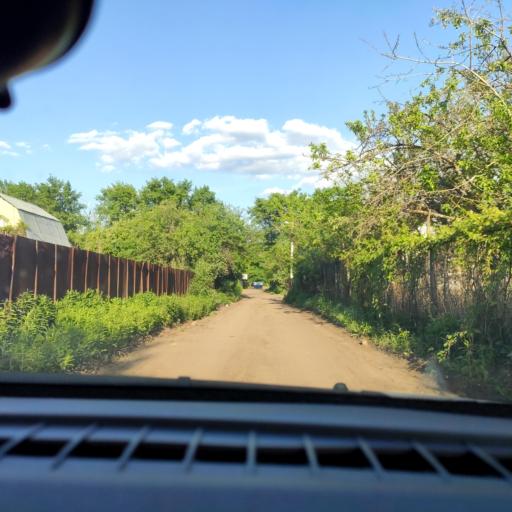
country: RU
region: Voronezj
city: Maslovka
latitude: 51.5216
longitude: 39.2374
